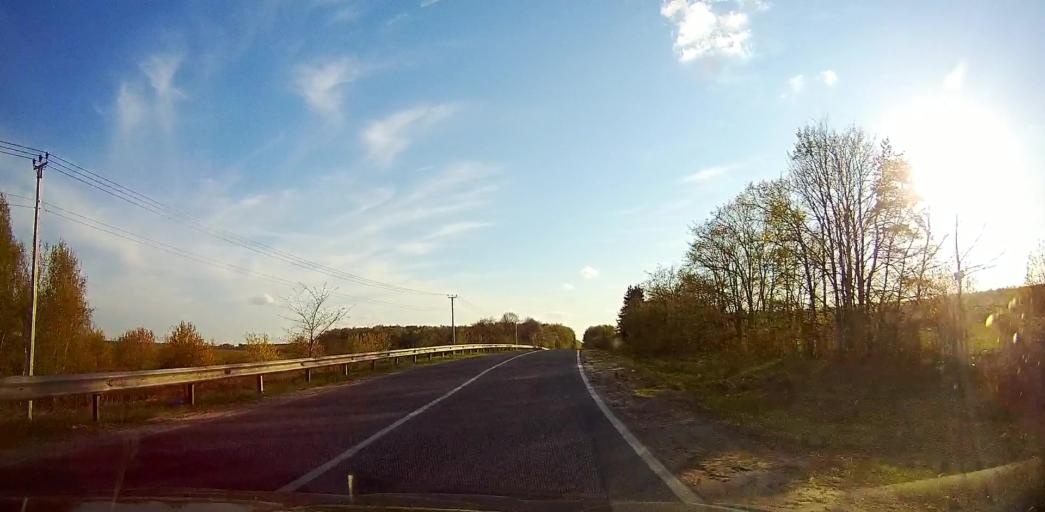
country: RU
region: Moskovskaya
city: Bronnitsy
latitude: 55.2953
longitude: 38.2122
